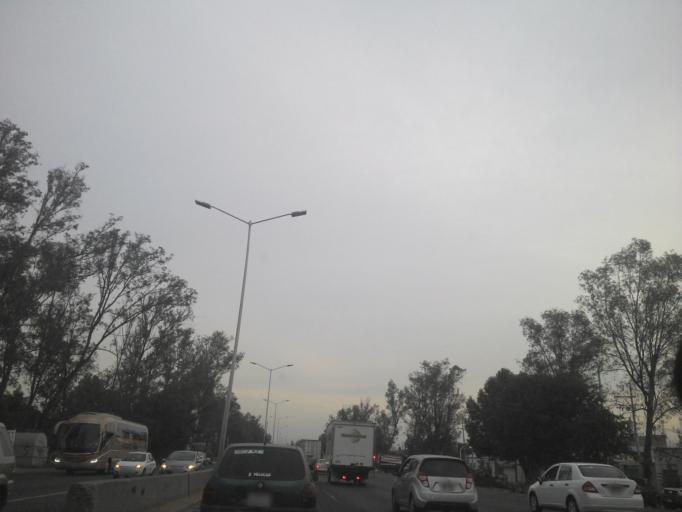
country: MX
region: Jalisco
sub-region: Tlajomulco de Zuniga
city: Palomar
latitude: 20.6224
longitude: -103.4321
